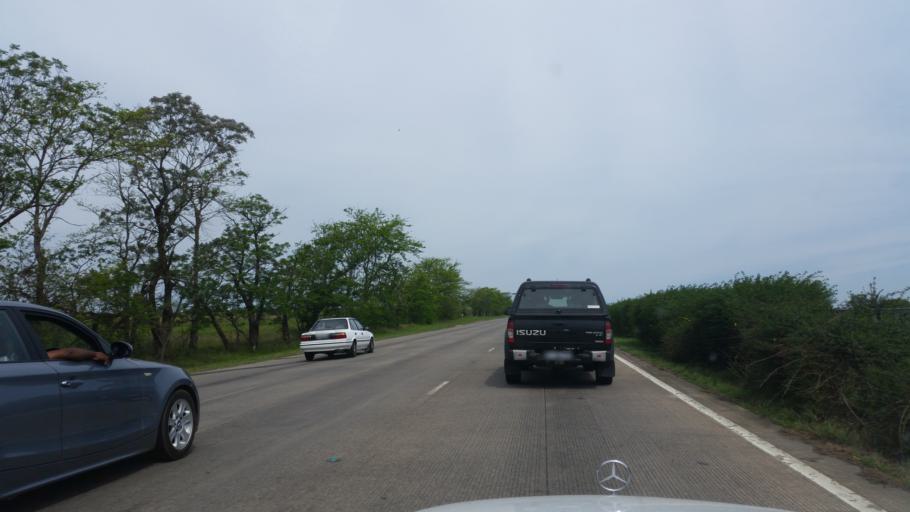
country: ZA
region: KwaZulu-Natal
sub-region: uMgungundlovu District Municipality
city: Camperdown
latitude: -29.6771
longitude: 30.4700
